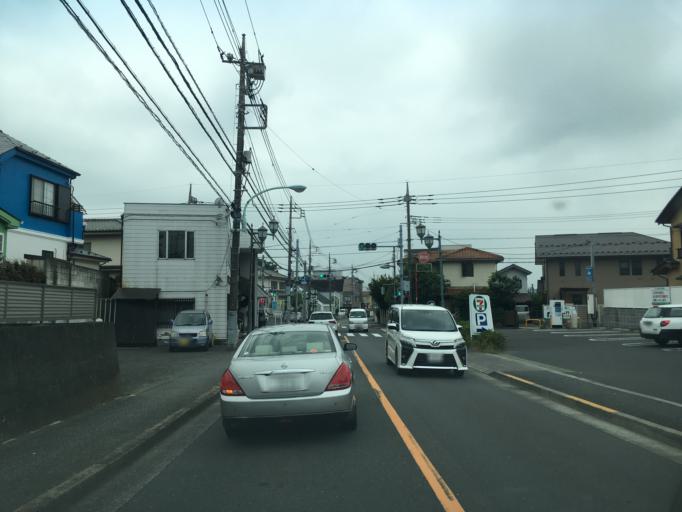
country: JP
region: Tokyo
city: Hino
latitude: 35.7270
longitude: 139.4001
